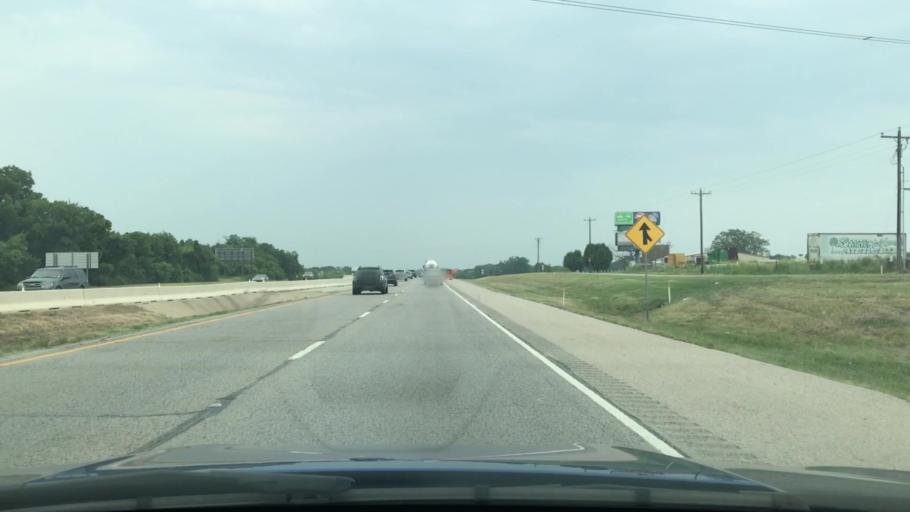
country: US
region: Texas
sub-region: Dallas County
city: Sunnyvale
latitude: 32.7769
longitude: -96.5155
